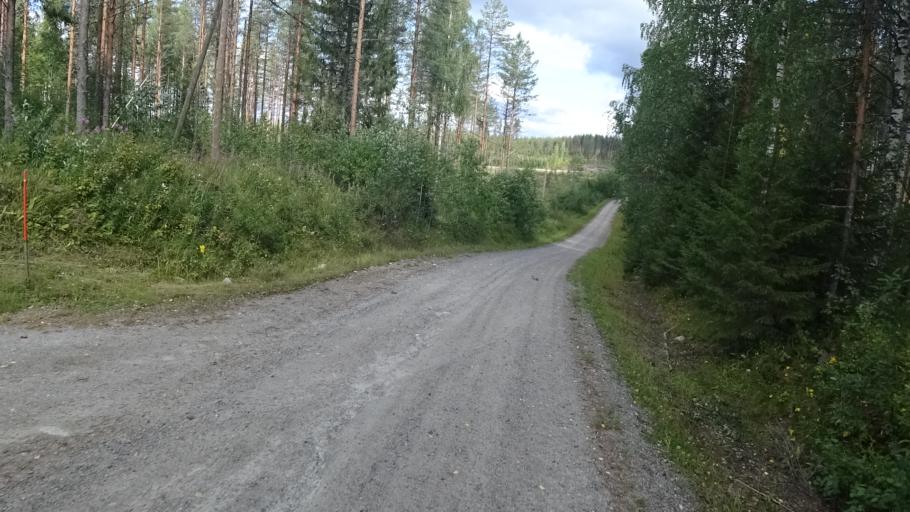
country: FI
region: North Karelia
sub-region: Joensuu
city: Ilomantsi
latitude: 62.6223
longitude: 31.2478
